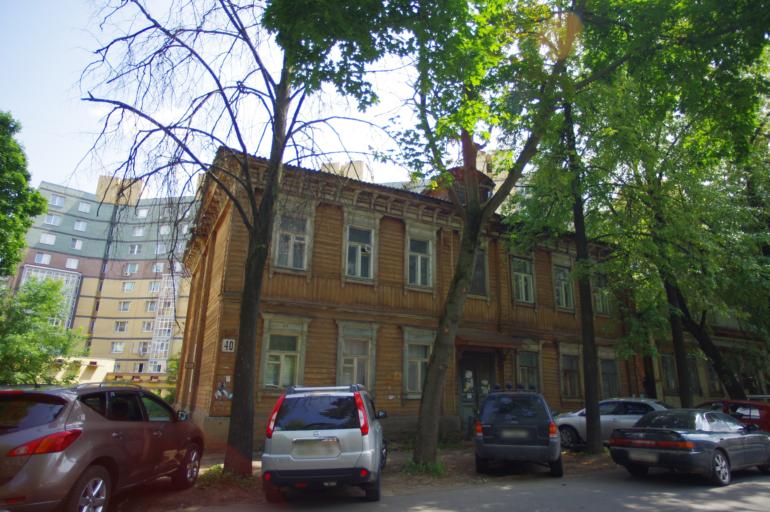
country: RU
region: Nizjnij Novgorod
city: Nizhniy Novgorod
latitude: 56.3103
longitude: 43.9938
